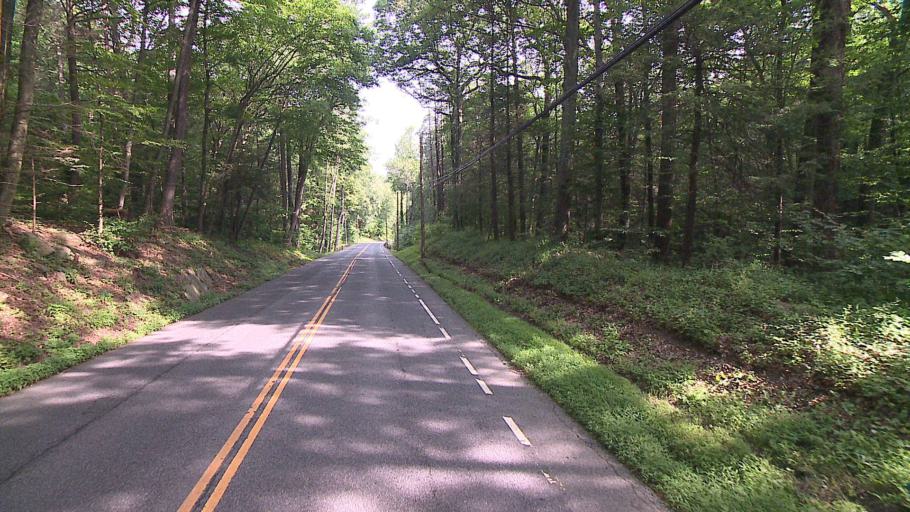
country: US
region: Connecticut
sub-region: Fairfield County
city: Sherman
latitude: 41.5656
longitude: -73.5071
